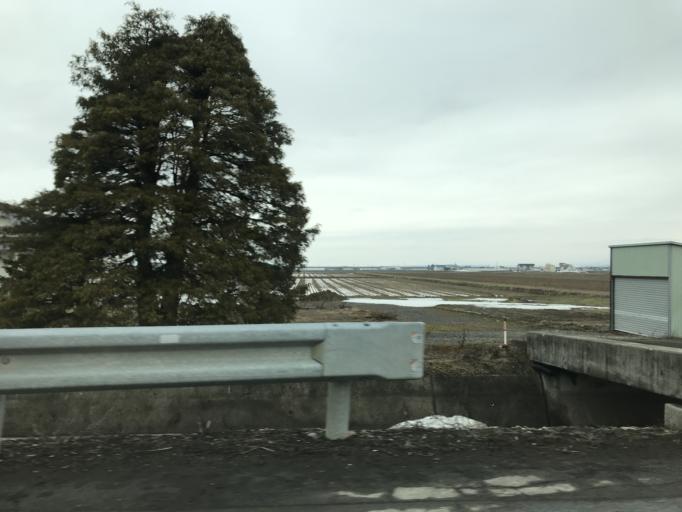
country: JP
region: Hokkaido
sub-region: Asahikawa-shi
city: Asahikawa
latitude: 43.8313
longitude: 142.4250
